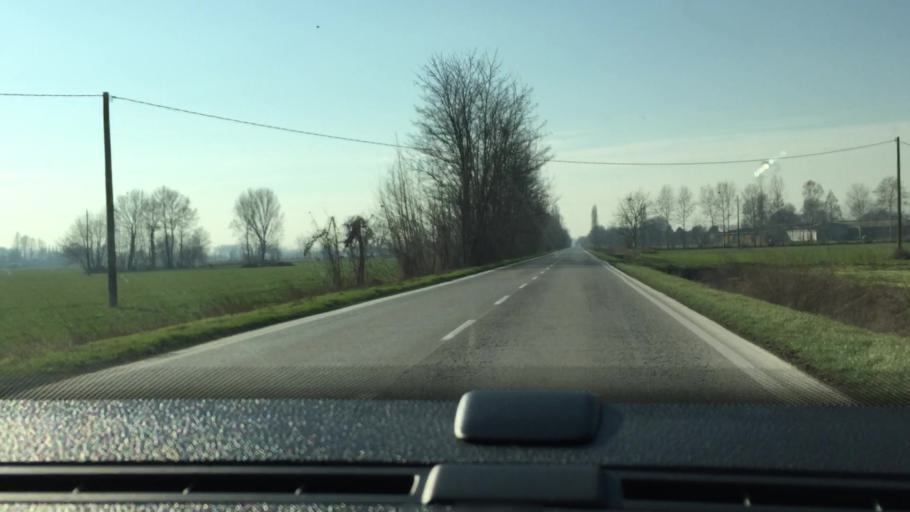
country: IT
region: Lombardy
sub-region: Provincia di Mantova
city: Goito
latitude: 45.2433
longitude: 10.6525
